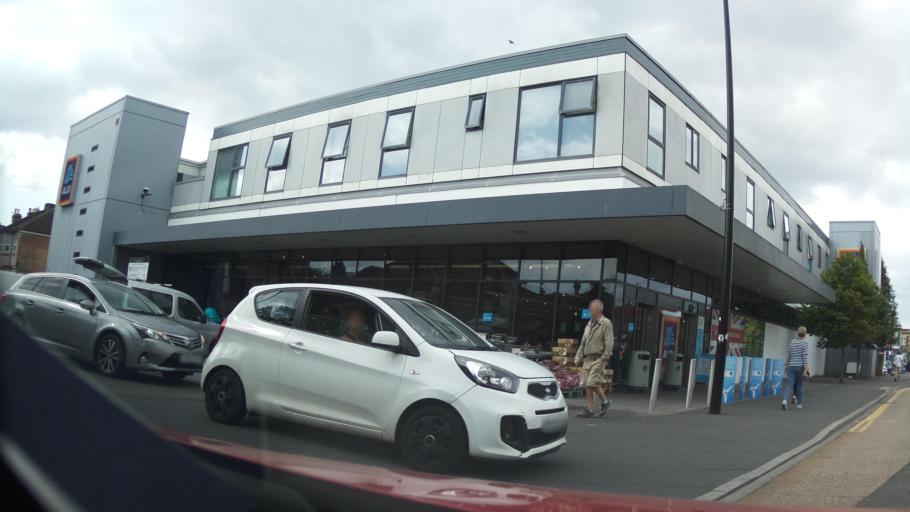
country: GB
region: England
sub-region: Bournemouth
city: Bournemouth
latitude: 50.7268
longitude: -1.8414
